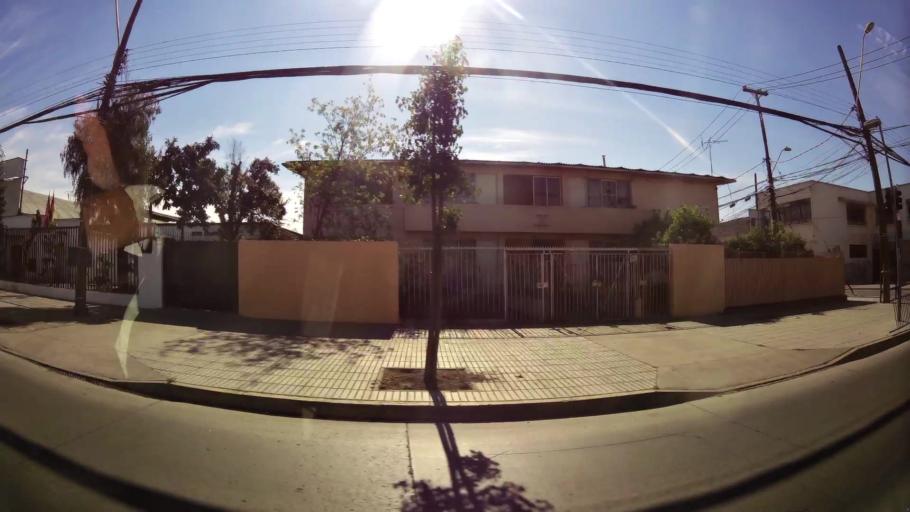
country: CL
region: Santiago Metropolitan
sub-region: Provincia de Santiago
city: Lo Prado
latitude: -33.4893
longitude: -70.7014
